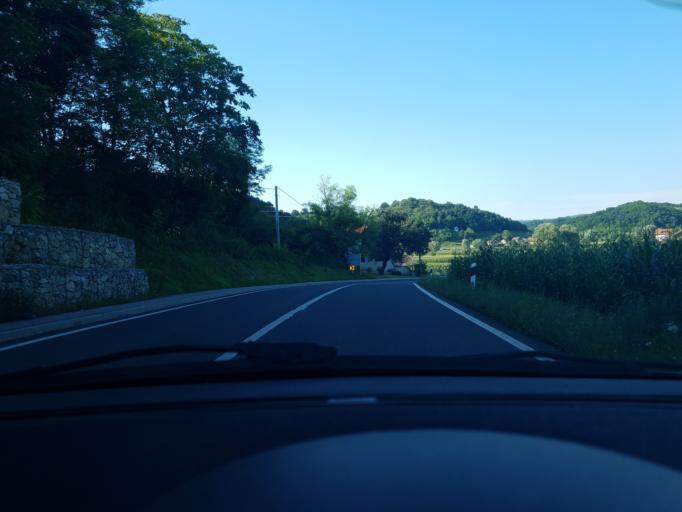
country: HR
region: Krapinsko-Zagorska
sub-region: Grad Krapina
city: Krapina
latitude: 46.1133
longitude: 15.9059
